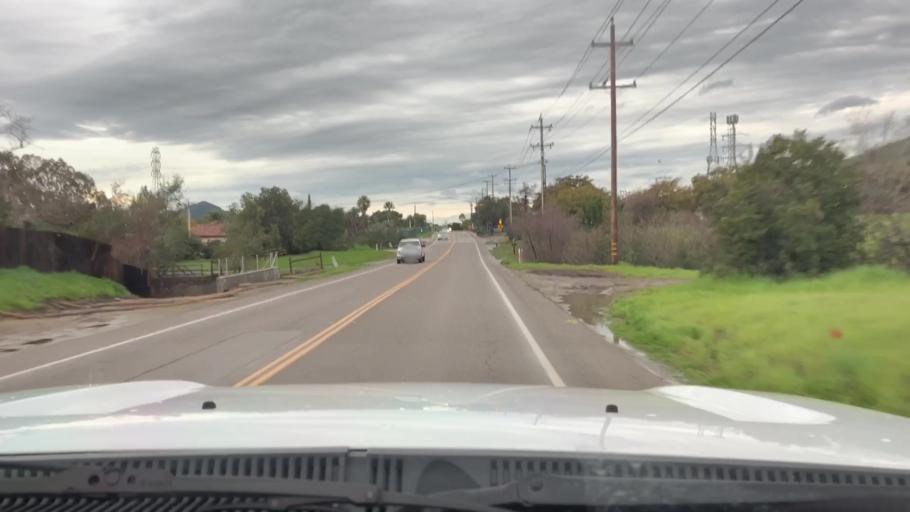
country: US
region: California
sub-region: San Luis Obispo County
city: San Luis Obispo
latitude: 35.2592
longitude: -120.6334
